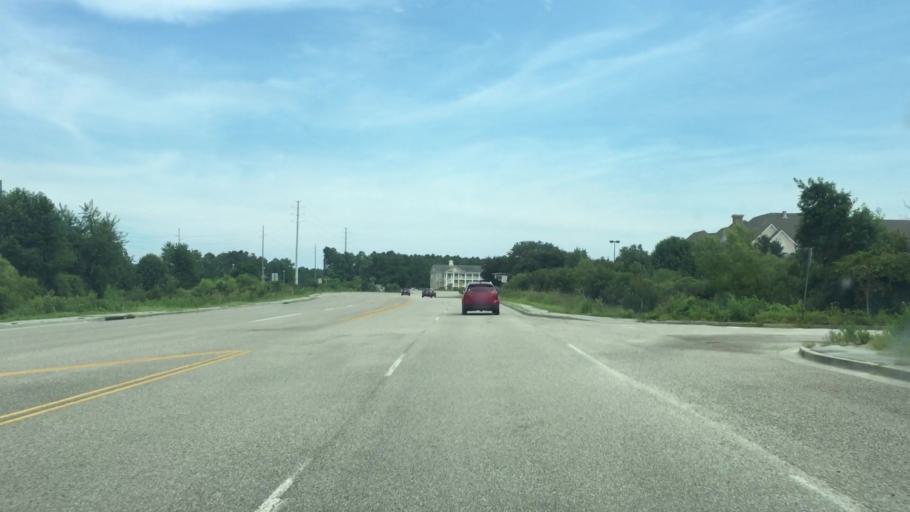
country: US
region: South Carolina
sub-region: Horry County
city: Forestbrook
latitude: 33.7154
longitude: -78.9298
